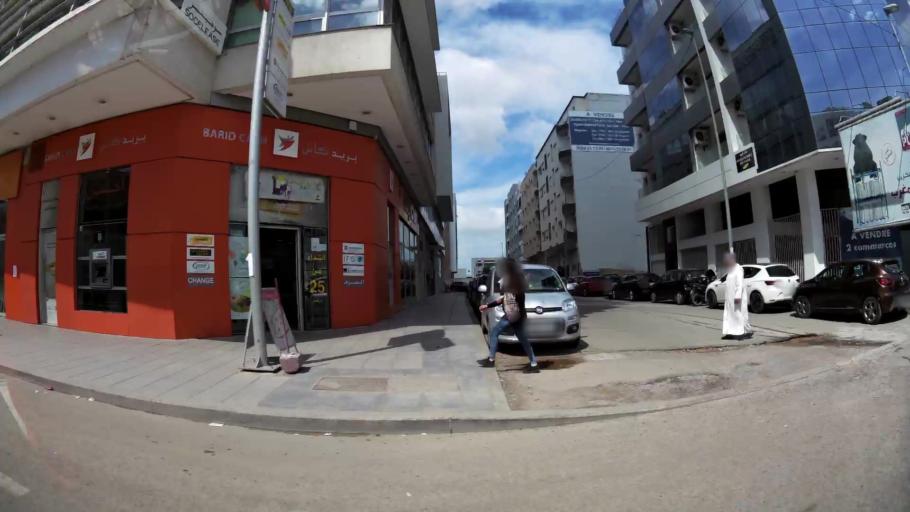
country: MA
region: Grand Casablanca
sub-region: Casablanca
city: Casablanca
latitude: 33.5711
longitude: -7.6261
